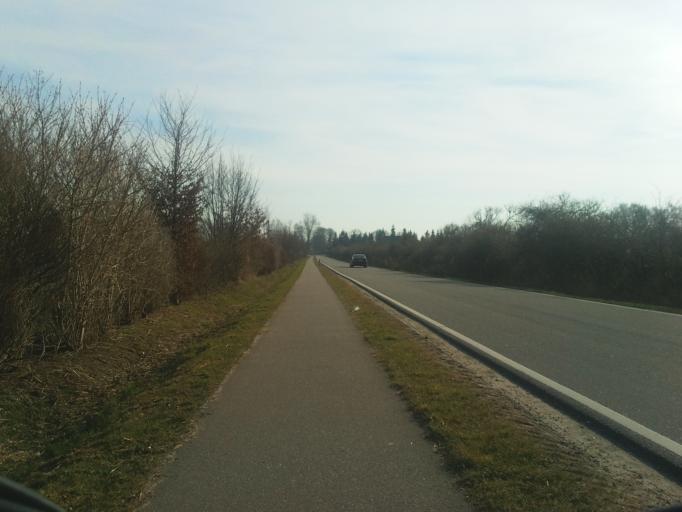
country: DE
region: Mecklenburg-Vorpommern
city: Lambrechtshagen
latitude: 54.1189
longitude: 12.0332
